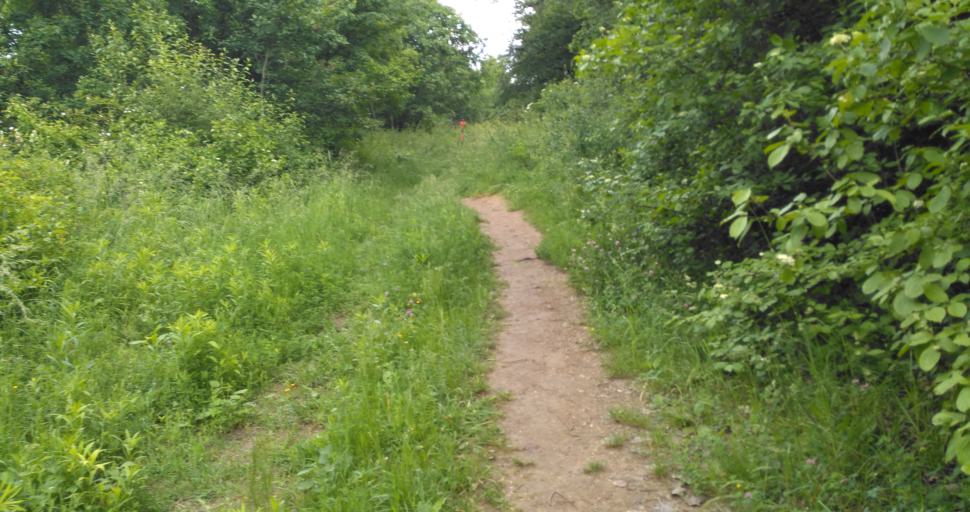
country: CZ
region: South Moravian
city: Podoli
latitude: 49.1917
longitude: 16.6744
